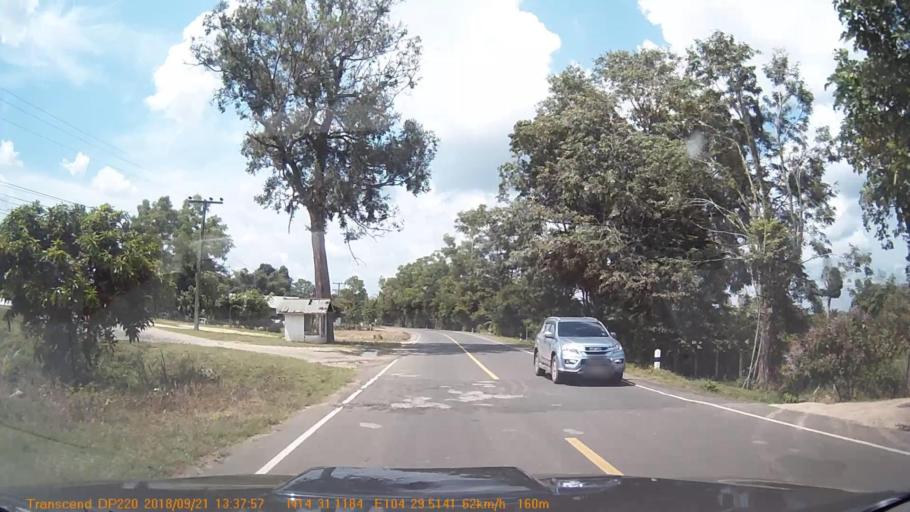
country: TH
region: Sisaket
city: Khun Han
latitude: 14.5187
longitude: 104.4919
